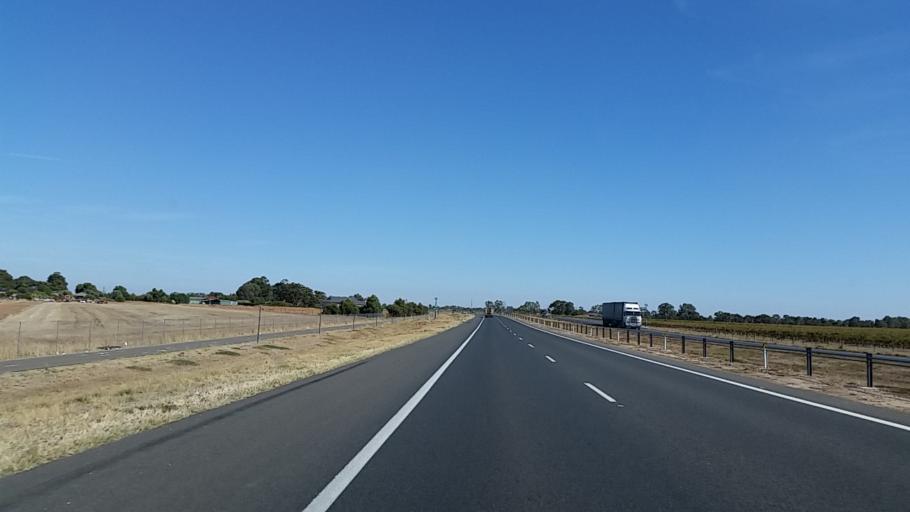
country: AU
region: South Australia
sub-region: Playford
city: Angle Vale
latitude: -34.6176
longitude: 138.6787
